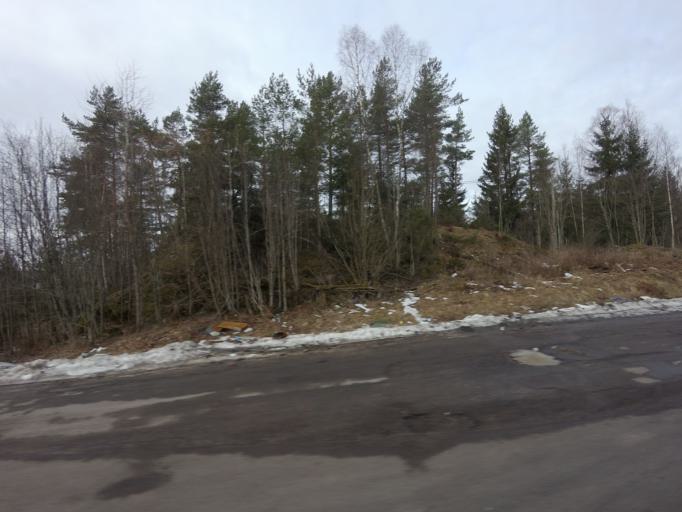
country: NO
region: Akershus
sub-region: Enebakk
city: Flateby
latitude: 59.8224
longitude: 11.2436
